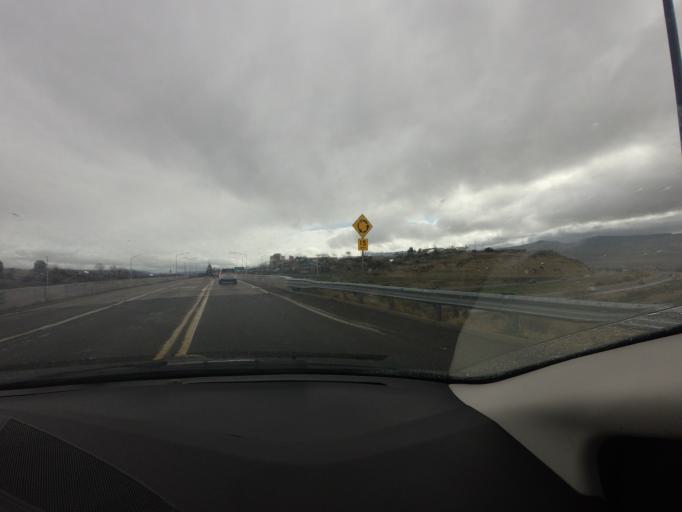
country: US
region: Arizona
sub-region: Yavapai County
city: Camp Verde
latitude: 34.6116
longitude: -111.8621
